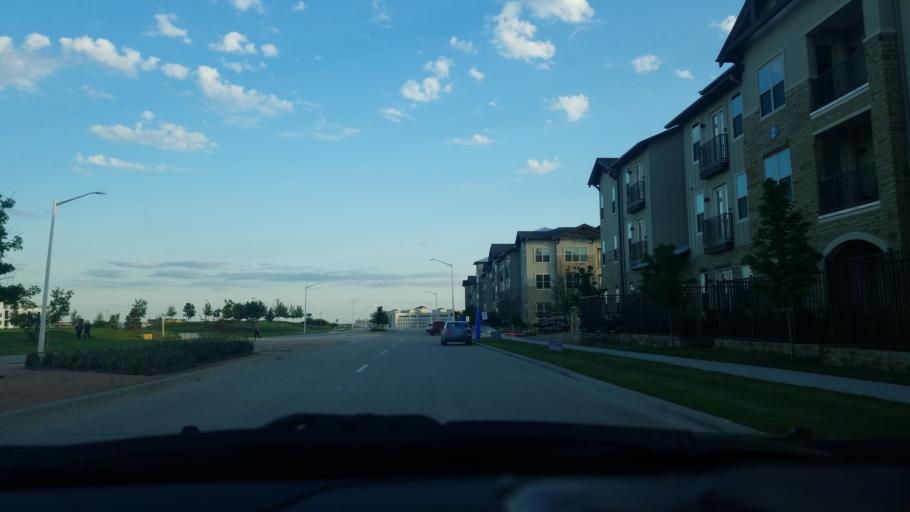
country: US
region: Texas
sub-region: Denton County
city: Denton
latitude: 33.2256
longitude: -97.1663
